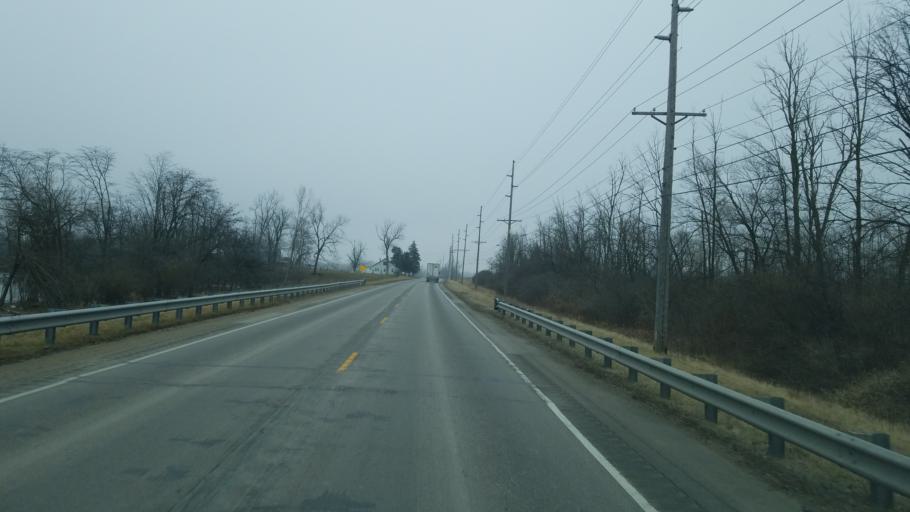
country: US
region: Indiana
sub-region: Adams County
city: Geneva
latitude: 40.5663
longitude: -84.9596
